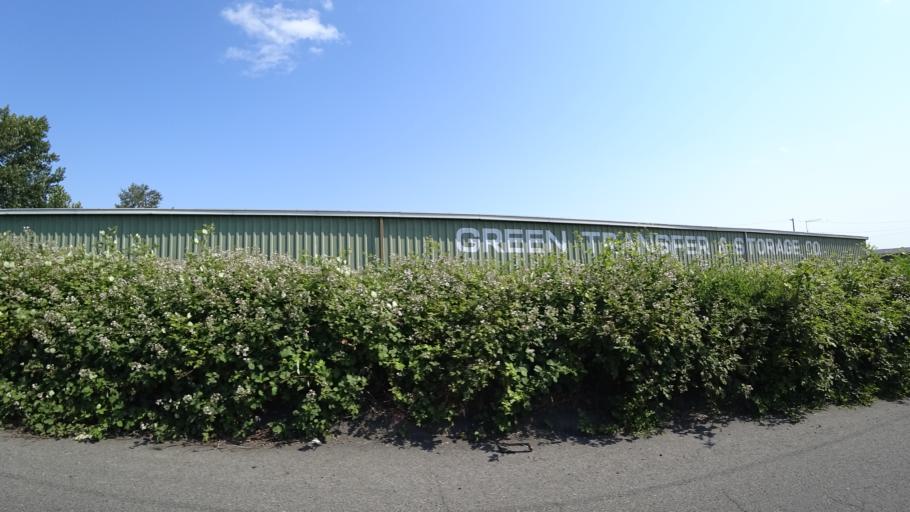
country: US
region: Washington
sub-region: Clark County
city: Vancouver
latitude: 45.5958
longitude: -122.7276
